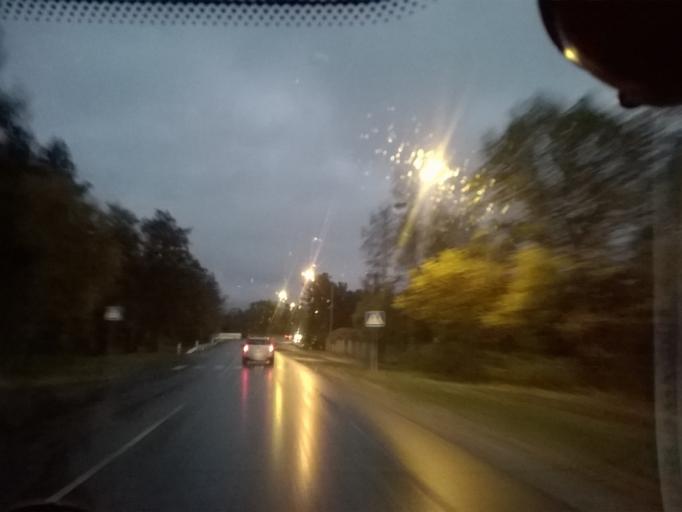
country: EE
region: Harju
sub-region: Viimsi vald
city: Rummu
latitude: 59.5206
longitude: 24.8065
